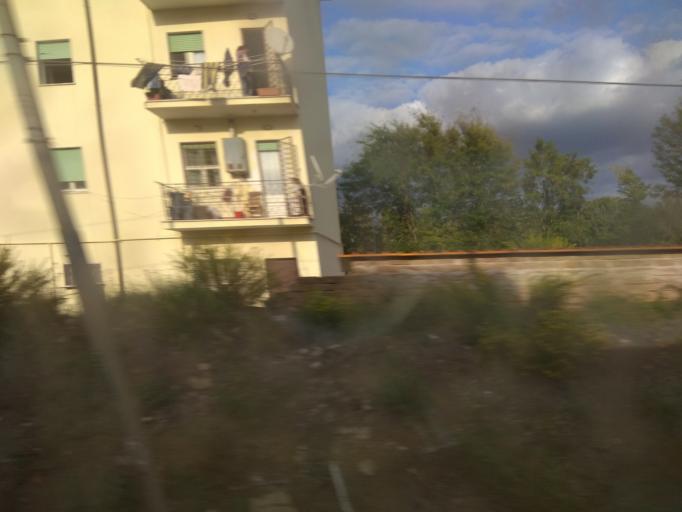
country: IT
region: Latium
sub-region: Citta metropolitana di Roma Capitale
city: Maccarese
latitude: 41.9122
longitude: 12.2037
